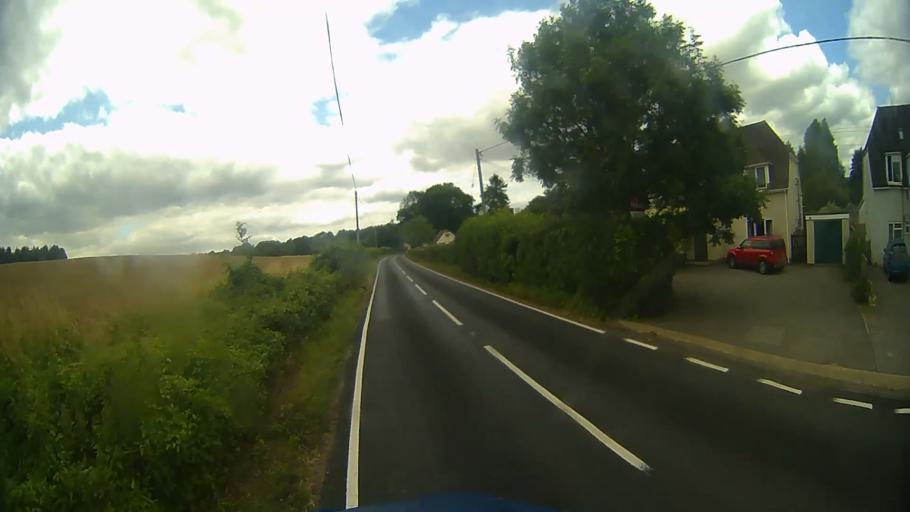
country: GB
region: England
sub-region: Hampshire
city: Four Marks
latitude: 51.1087
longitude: -1.1605
